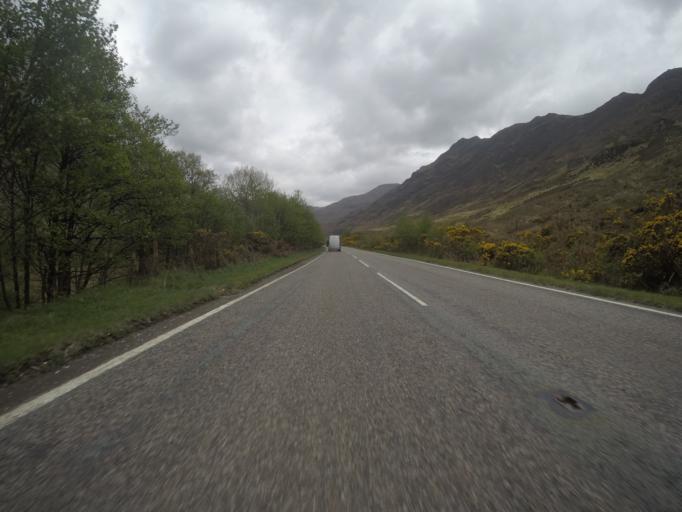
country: GB
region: Scotland
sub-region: Highland
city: Fort William
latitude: 57.1924
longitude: -5.3869
